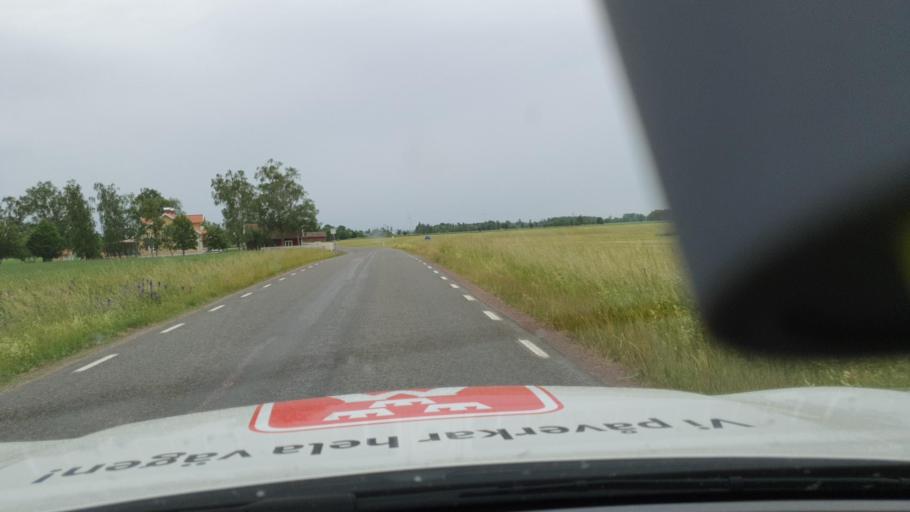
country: SE
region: Vaestra Goetaland
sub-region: Tidaholms Kommun
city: Olofstorp
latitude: 58.3295
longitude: 14.0594
